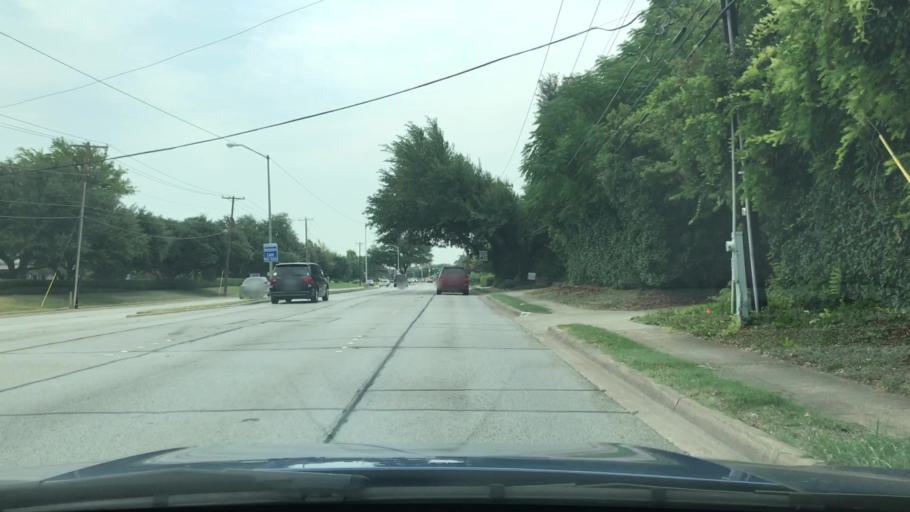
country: US
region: Texas
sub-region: Dallas County
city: Richardson
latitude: 32.9630
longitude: -96.7425
